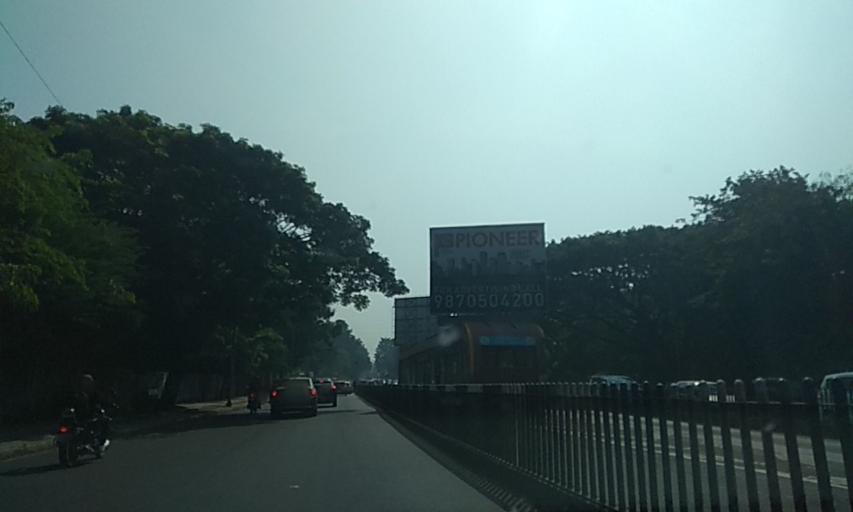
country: IN
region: Maharashtra
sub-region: Pune Division
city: Shivaji Nagar
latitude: 18.5457
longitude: 73.8759
